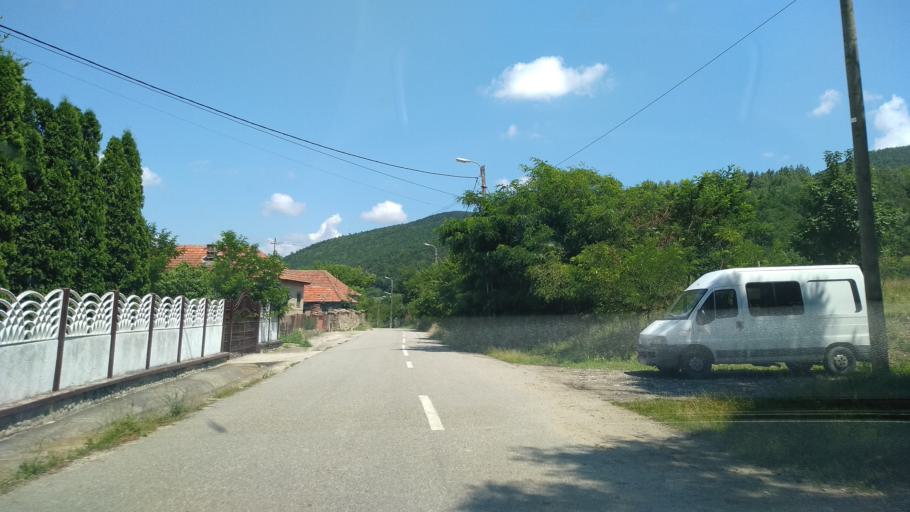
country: RO
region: Hunedoara
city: Berca
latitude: 45.6064
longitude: 23.0208
